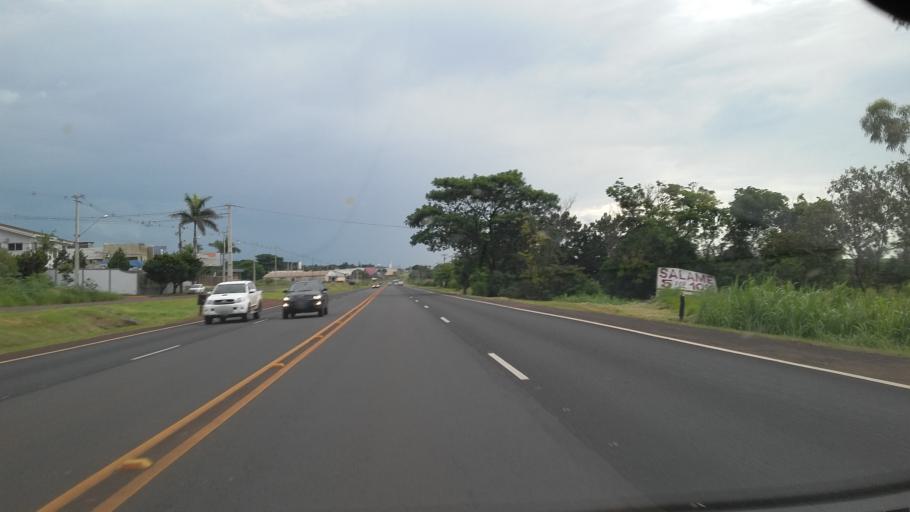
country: BR
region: Parana
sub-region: Arapongas
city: Arapongas
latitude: -23.3920
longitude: -51.4596
